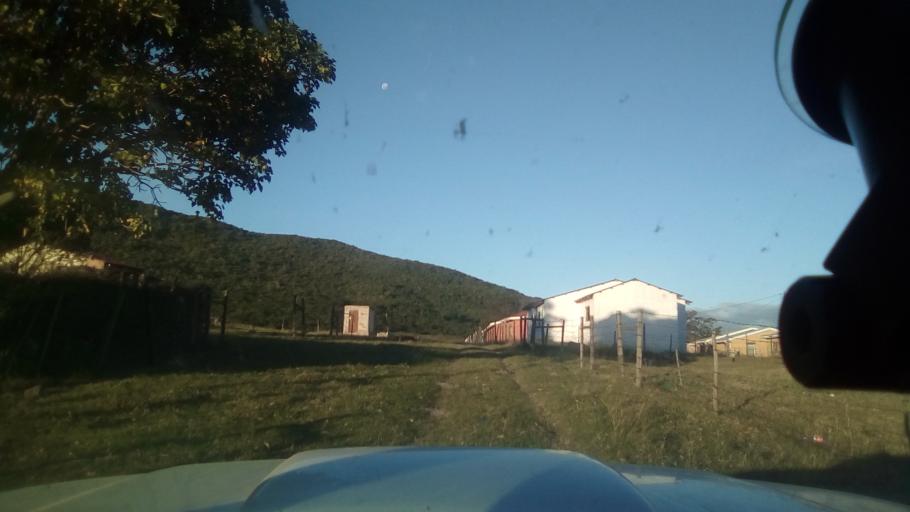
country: ZA
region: Eastern Cape
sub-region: Buffalo City Metropolitan Municipality
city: Bhisho
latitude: -32.7348
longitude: 27.3779
